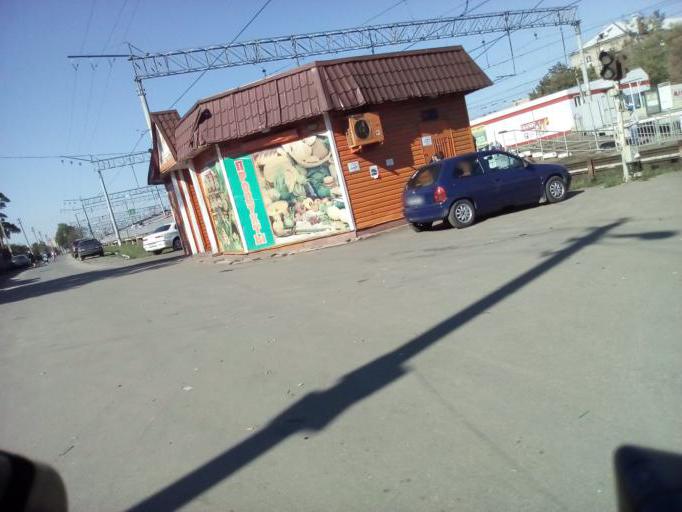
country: RU
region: Moskovskaya
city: Ramenskoye
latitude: 55.5595
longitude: 38.2410
